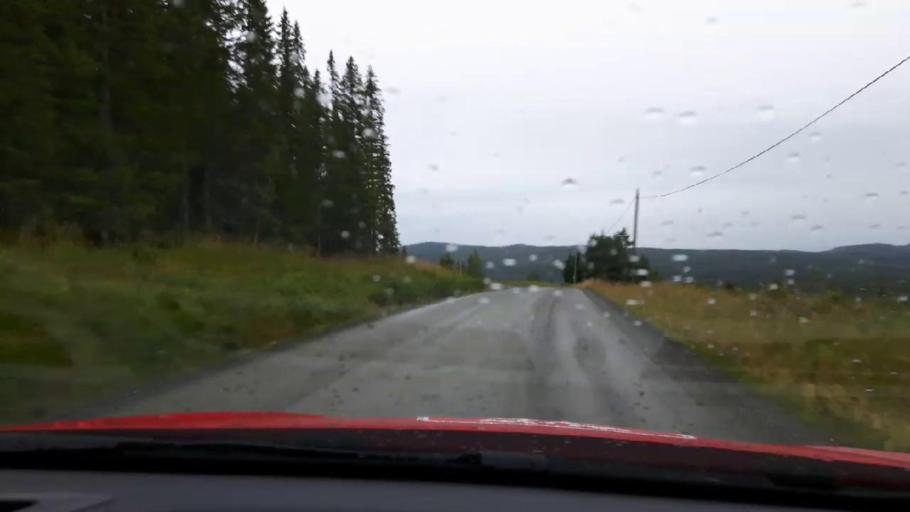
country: SE
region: Jaemtland
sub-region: Are Kommun
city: Are
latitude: 63.4204
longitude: 12.8236
